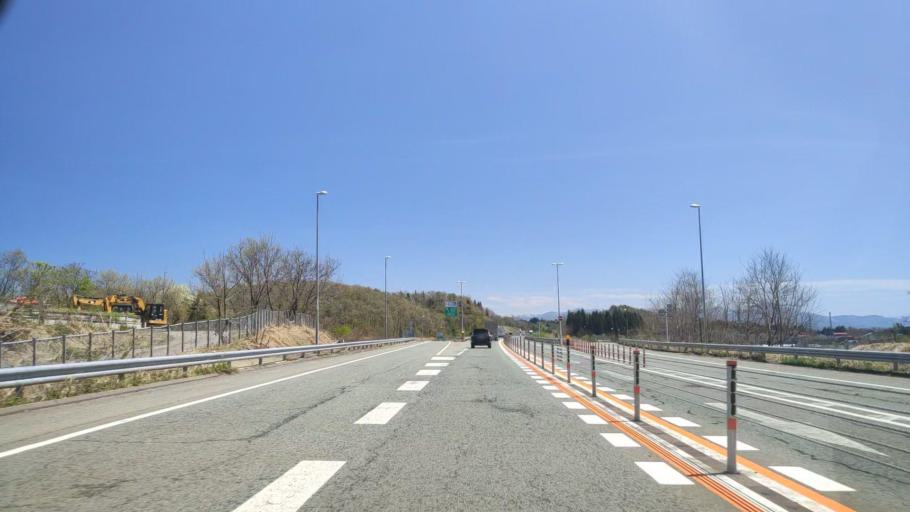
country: JP
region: Yamagata
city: Obanazawa
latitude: 38.6608
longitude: 140.3616
